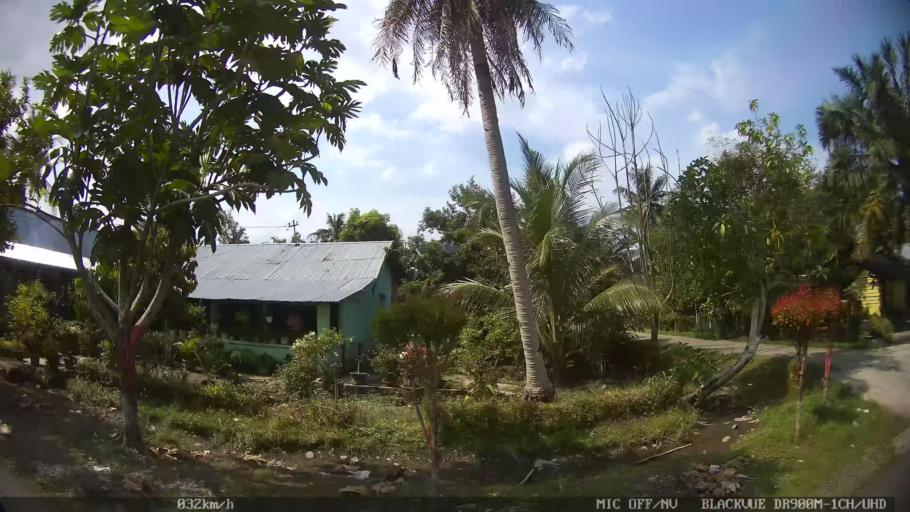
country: ID
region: North Sumatra
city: Binjai
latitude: 3.6354
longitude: 98.5196
